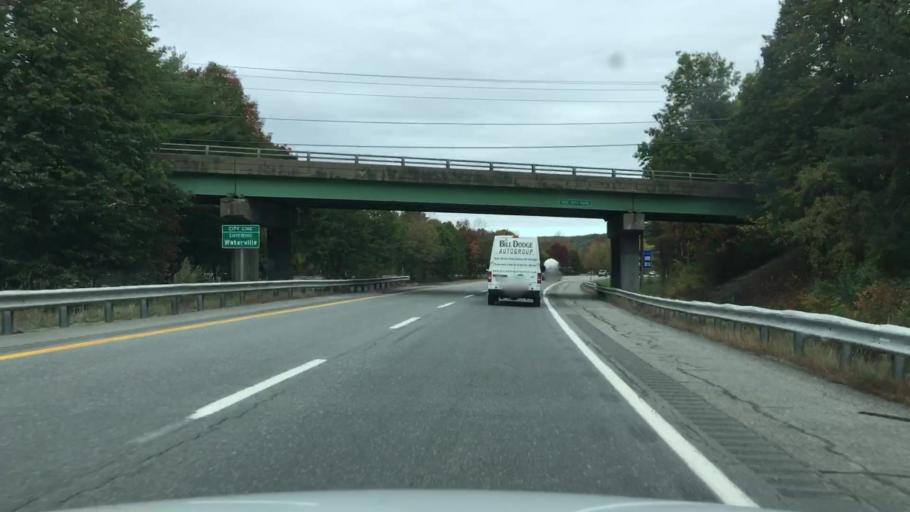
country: US
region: Maine
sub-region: Kennebec County
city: Waterville
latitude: 44.5658
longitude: -69.6692
